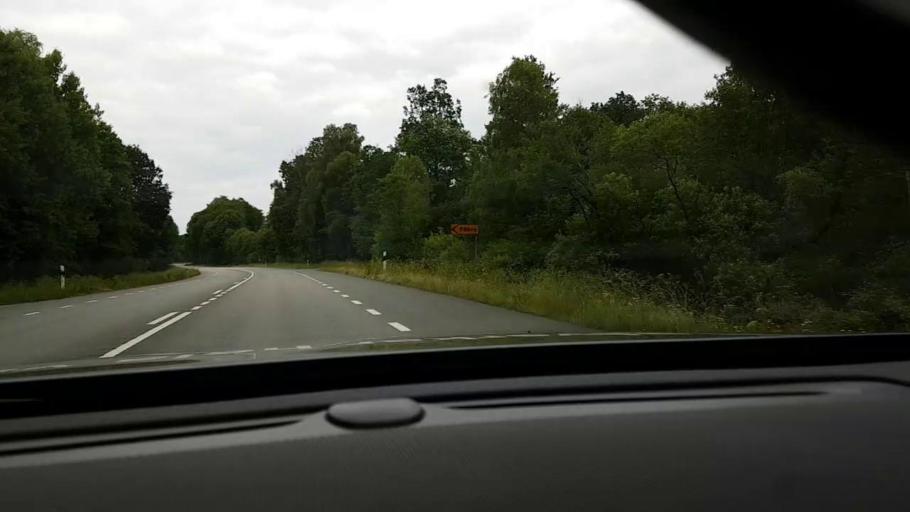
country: SE
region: Skane
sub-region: Hassleholms Kommun
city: Tormestorp
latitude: 56.1015
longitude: 13.7785
